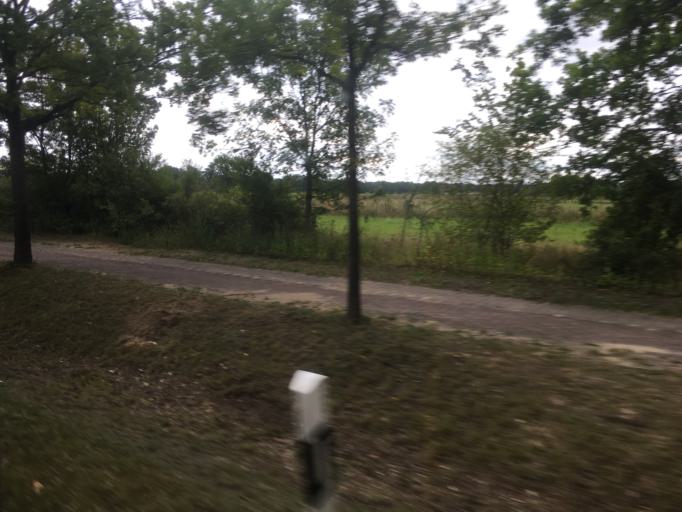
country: DE
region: Berlin
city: Wilhelmstadt
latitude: 52.5032
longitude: 13.1603
